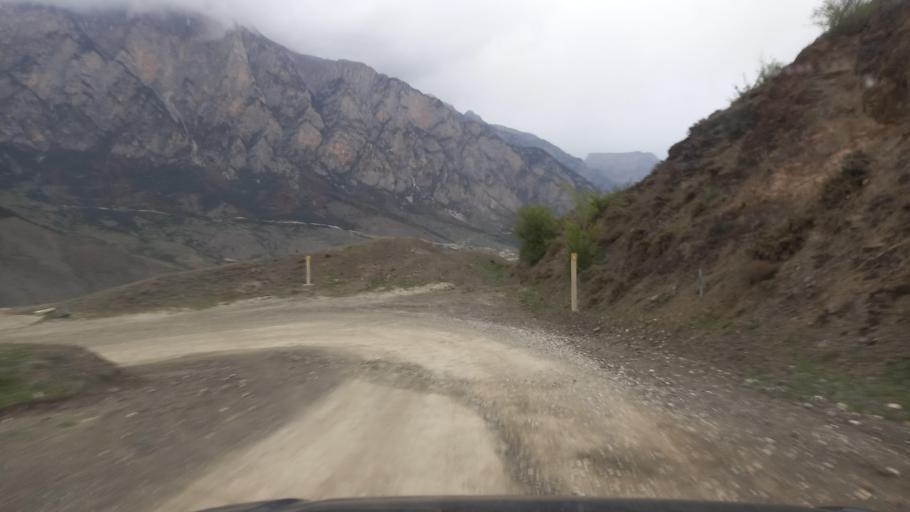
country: RU
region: North Ossetia
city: Mizur
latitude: 42.8597
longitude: 44.1581
